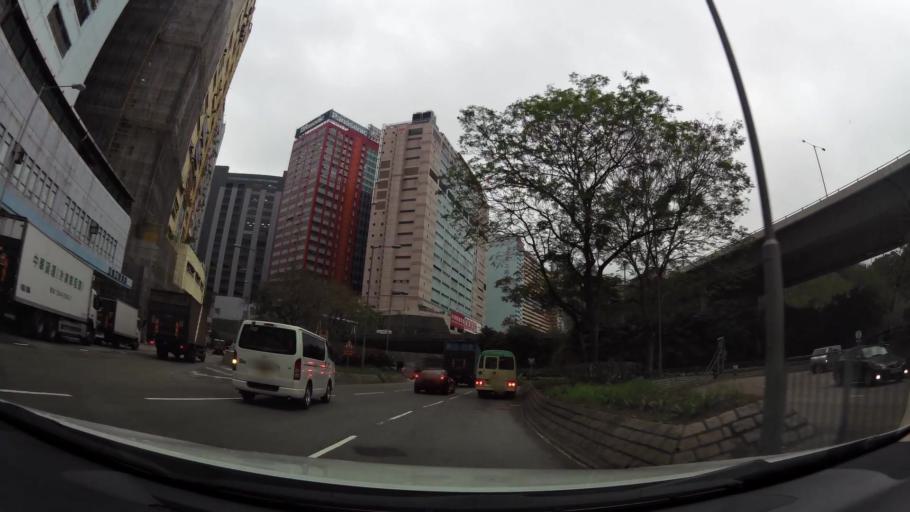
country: HK
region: Tsuen Wan
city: Tsuen Wan
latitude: 22.3639
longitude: 114.1173
